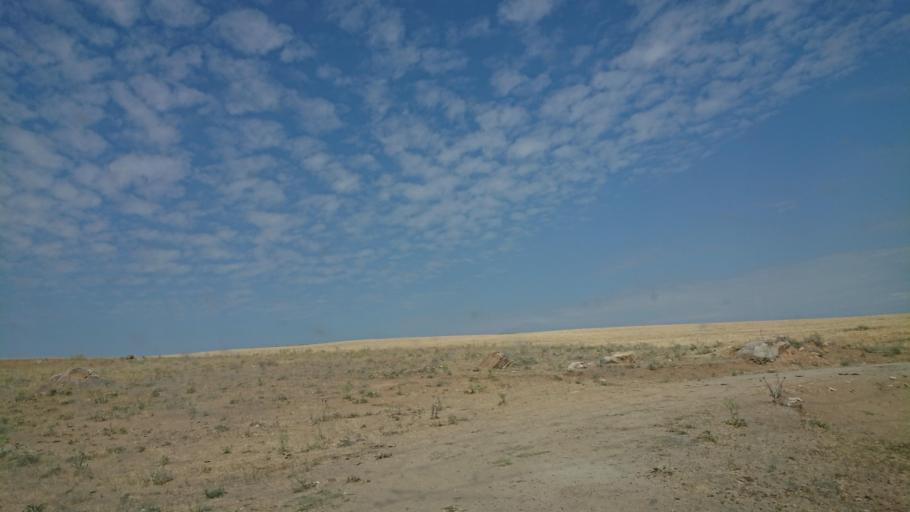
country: TR
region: Aksaray
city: Agacoren
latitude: 38.9489
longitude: 33.9125
